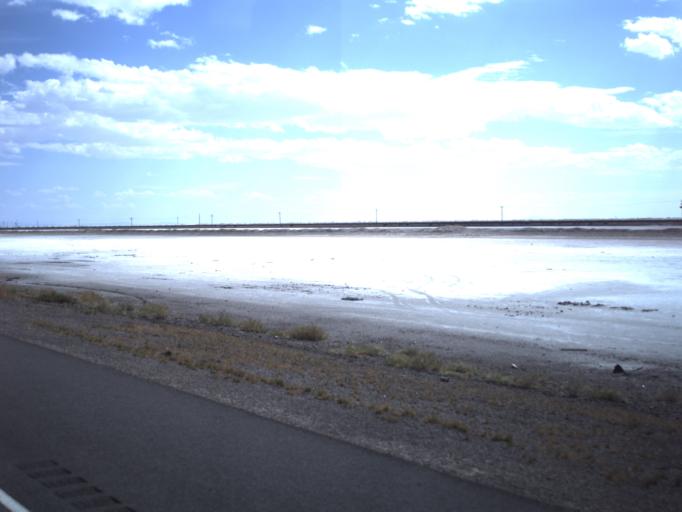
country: US
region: Utah
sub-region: Tooele County
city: Wendover
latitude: 40.7399
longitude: -113.9228
